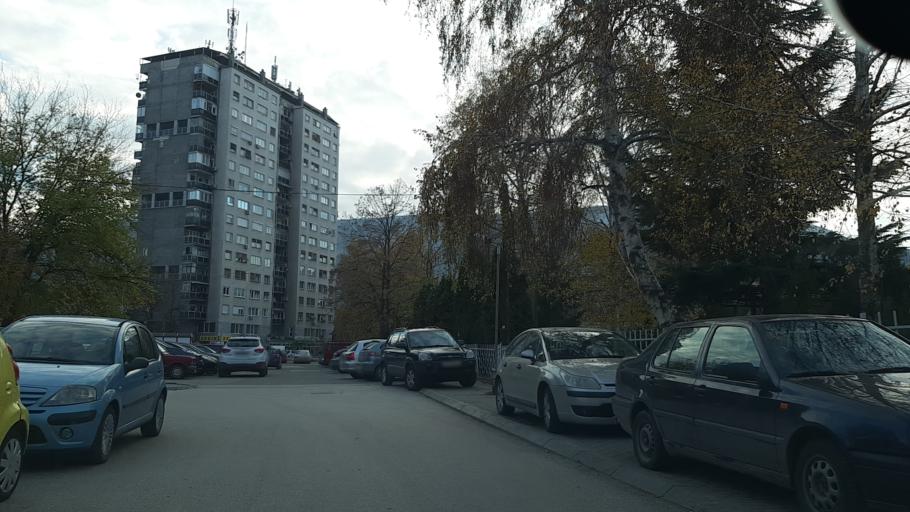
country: MK
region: Karpos
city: Skopje
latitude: 41.9816
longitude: 21.4422
